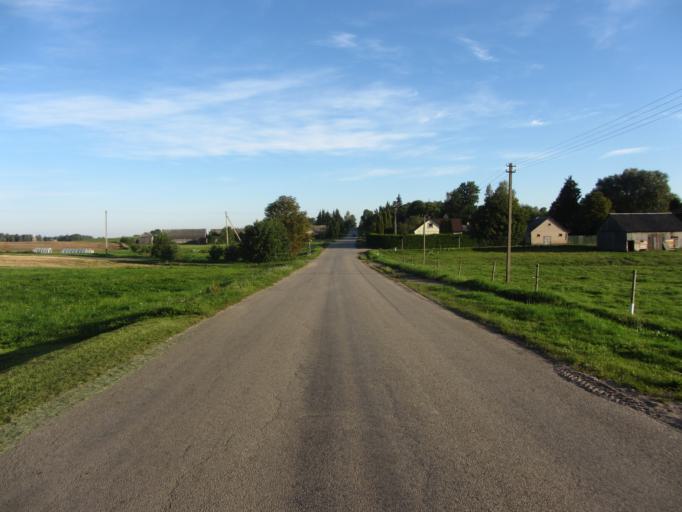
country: LT
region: Alytaus apskritis
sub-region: Alytus
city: Alytus
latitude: 54.3643
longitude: 23.8848
